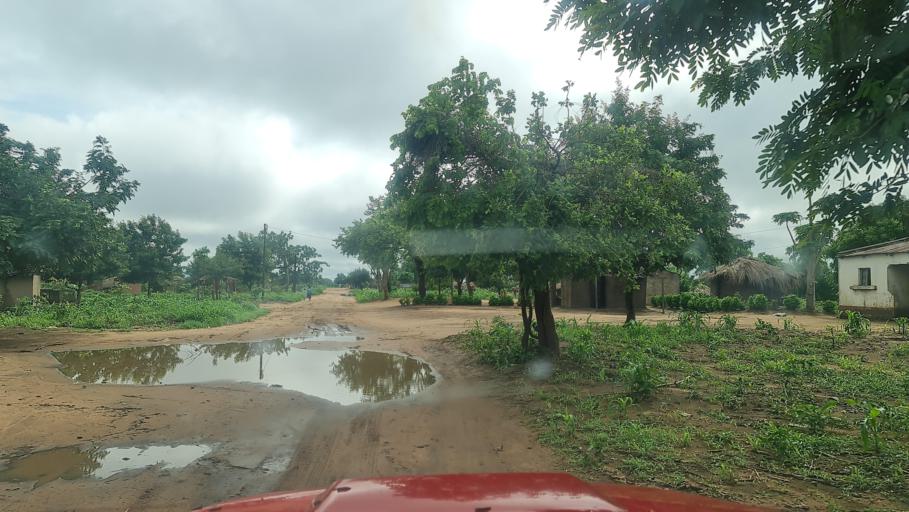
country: MW
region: Southern Region
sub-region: Nsanje District
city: Nsanje
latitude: -17.2215
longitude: 35.6697
